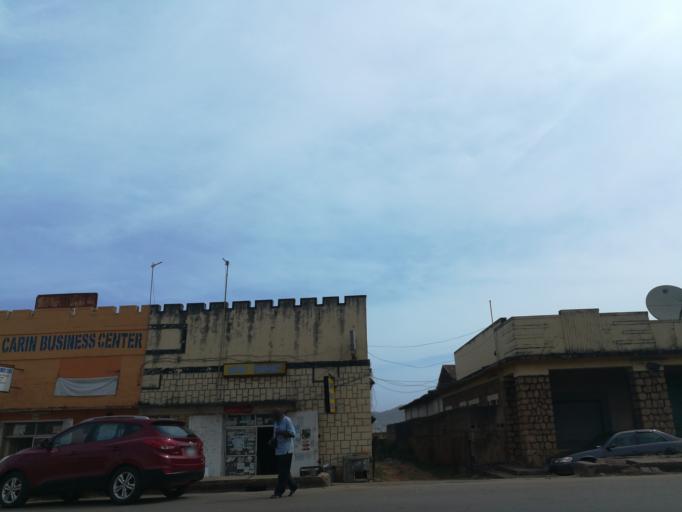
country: NG
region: Plateau
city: Jos
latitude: 9.9136
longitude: 8.8901
